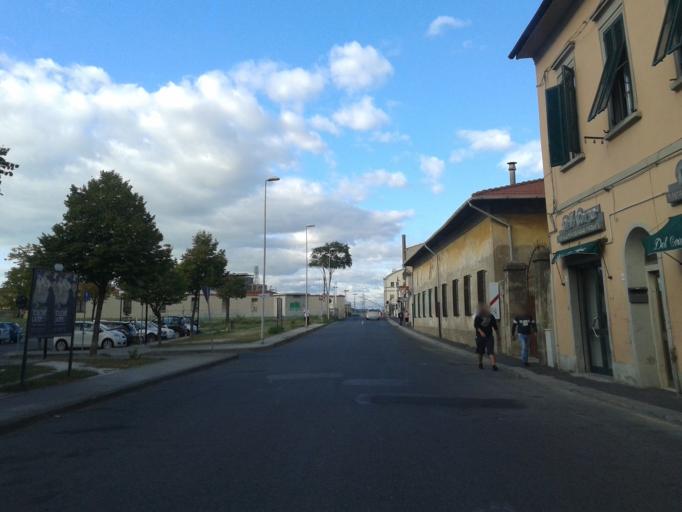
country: IT
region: Tuscany
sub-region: Provincia di Livorno
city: Livorno
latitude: 43.5611
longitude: 10.3124
